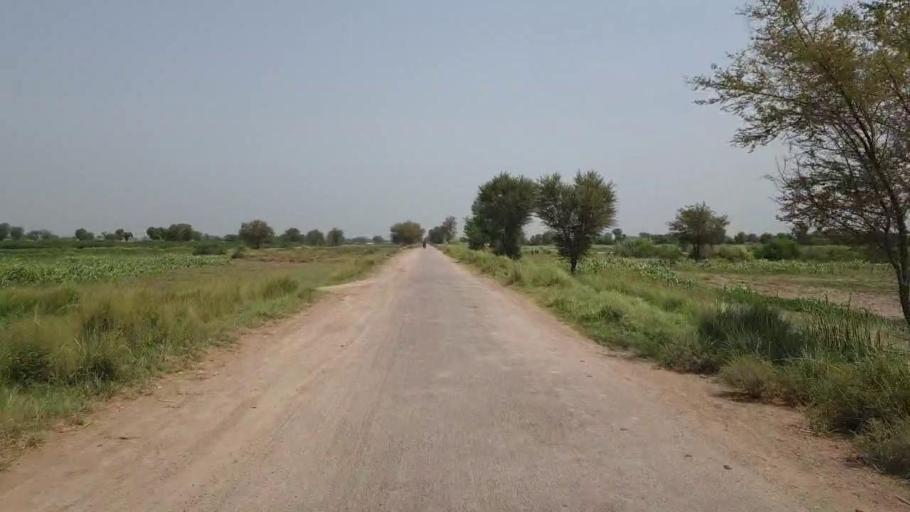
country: PK
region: Sindh
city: Nawabshah
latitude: 26.2611
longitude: 68.3188
